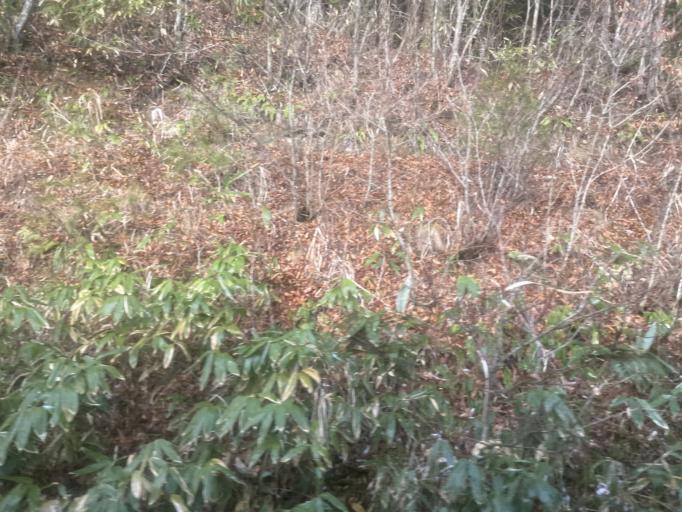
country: JP
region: Aomori
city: Goshogawara
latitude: 41.0774
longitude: 140.5367
